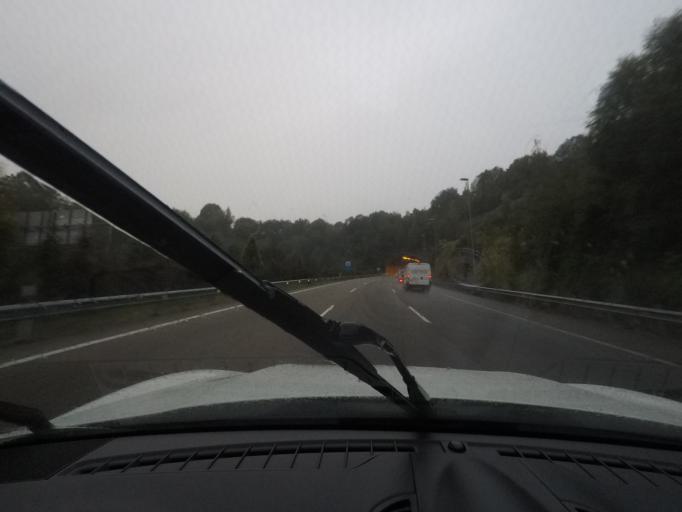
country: ES
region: Asturias
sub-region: Province of Asturias
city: Oviedo
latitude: 43.3421
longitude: -5.8778
